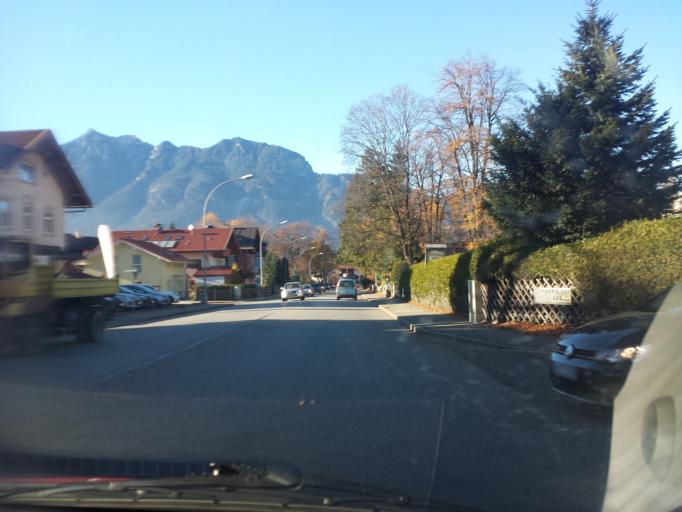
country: DE
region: Bavaria
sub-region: Upper Bavaria
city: Garmisch-Partenkirchen
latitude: 47.4876
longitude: 11.1160
